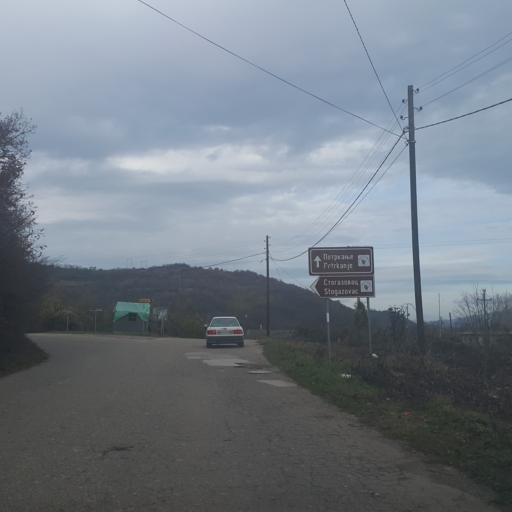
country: RS
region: Central Serbia
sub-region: Zajecarski Okrug
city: Knjazevac
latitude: 43.5811
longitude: 22.2476
